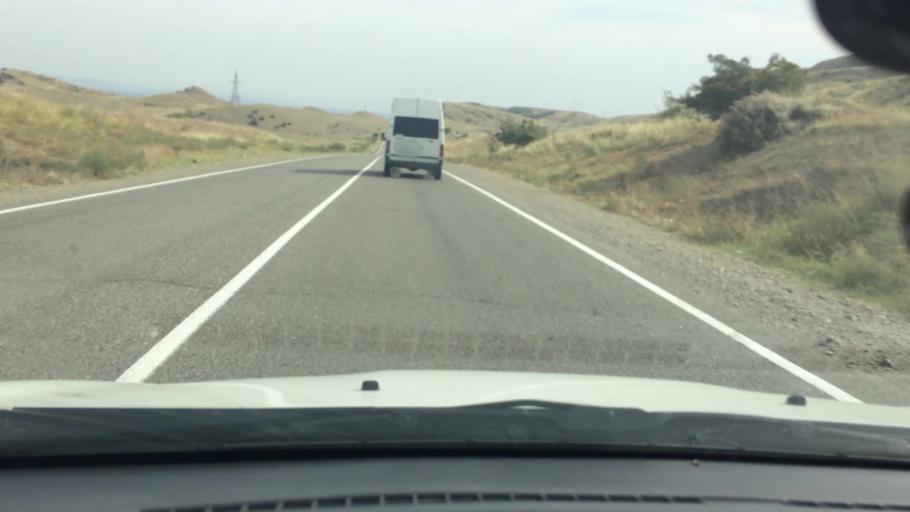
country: GE
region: Kvemo Kartli
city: Rust'avi
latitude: 41.5356
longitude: 44.9789
